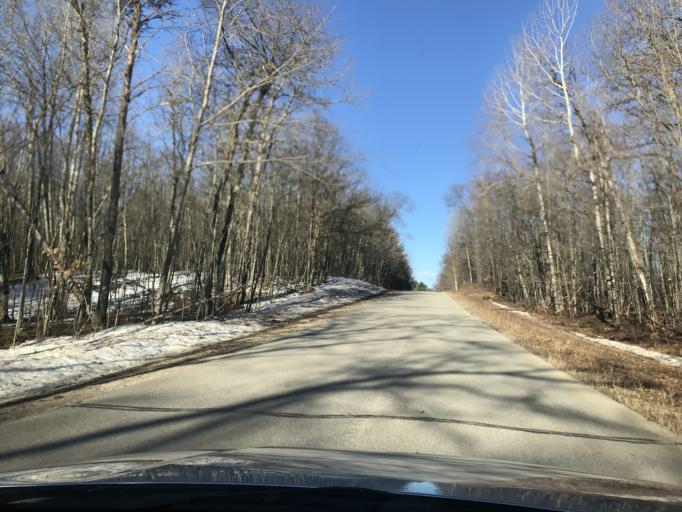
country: US
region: Wisconsin
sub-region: Marinette County
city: Niagara
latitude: 45.3905
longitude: -88.0734
